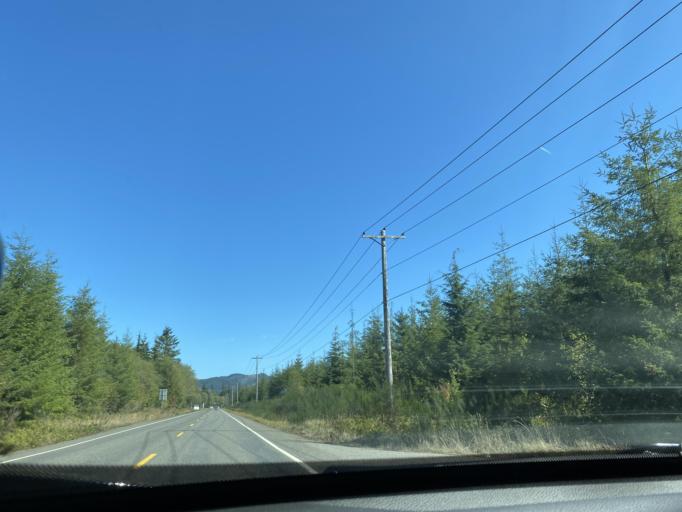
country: US
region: Washington
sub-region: Clallam County
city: Forks
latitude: 47.9648
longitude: -124.4156
